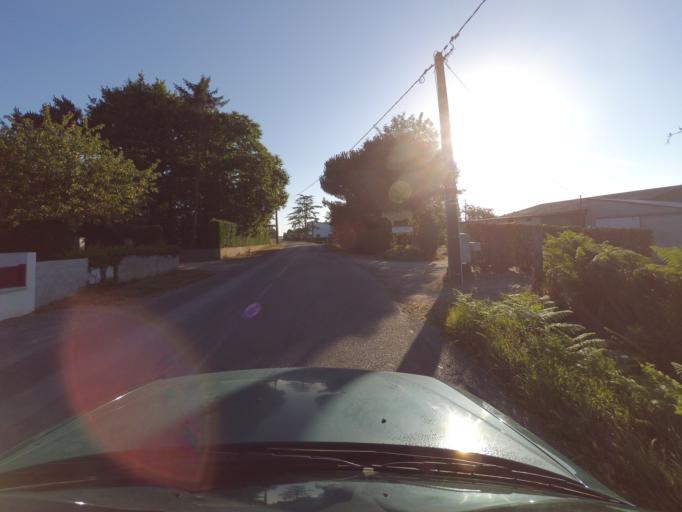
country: FR
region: Pays de la Loire
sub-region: Departement de la Loire-Atlantique
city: Montbert
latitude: 47.0643
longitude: -1.4787
